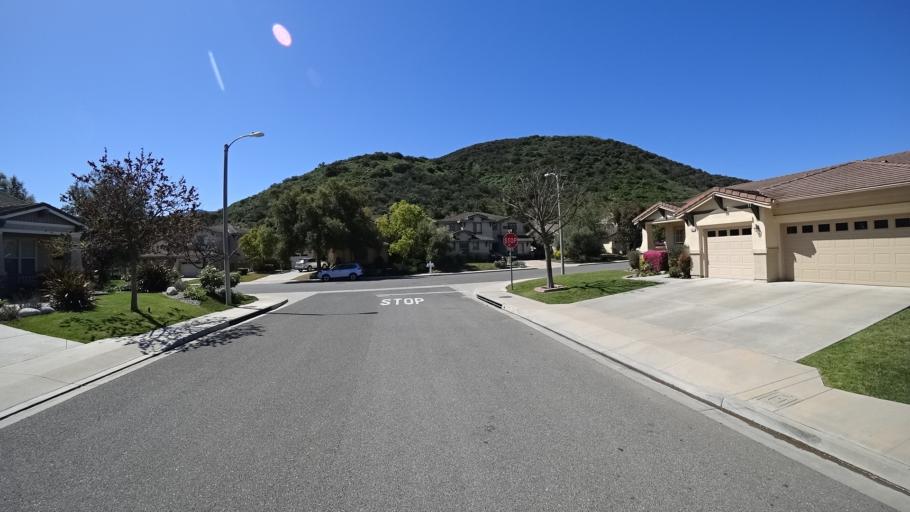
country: US
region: California
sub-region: Ventura County
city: Casa Conejo
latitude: 34.1652
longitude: -118.9747
